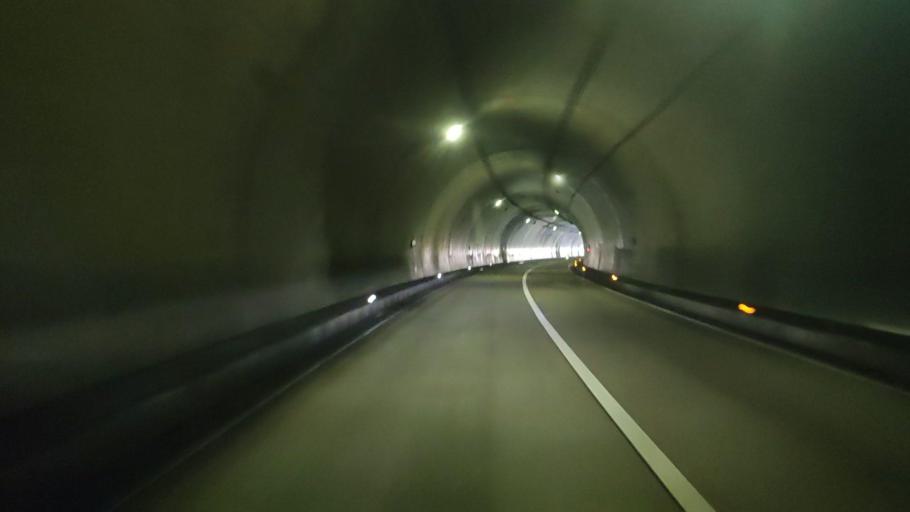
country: JP
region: Wakayama
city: Shingu
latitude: 33.8583
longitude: 135.8519
